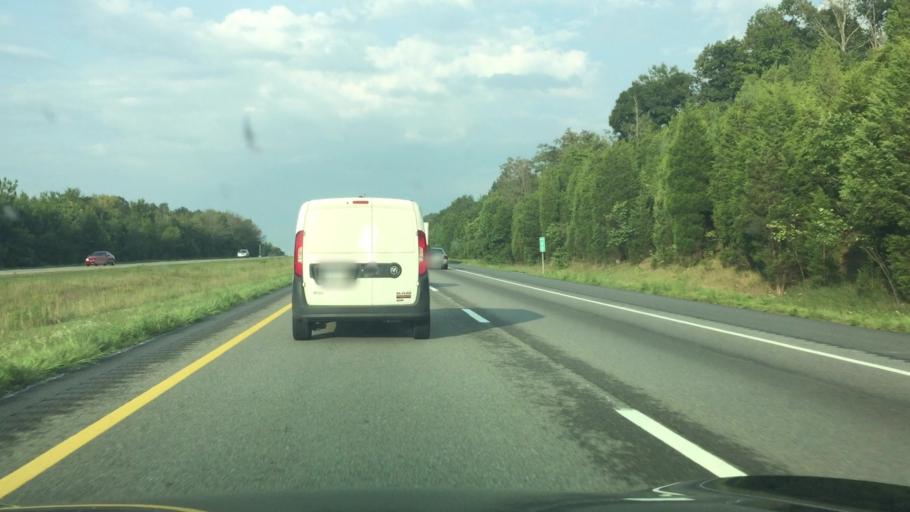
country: US
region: Tennessee
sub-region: Hawkins County
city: Surgoinsville
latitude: 36.3474
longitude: -82.7767
